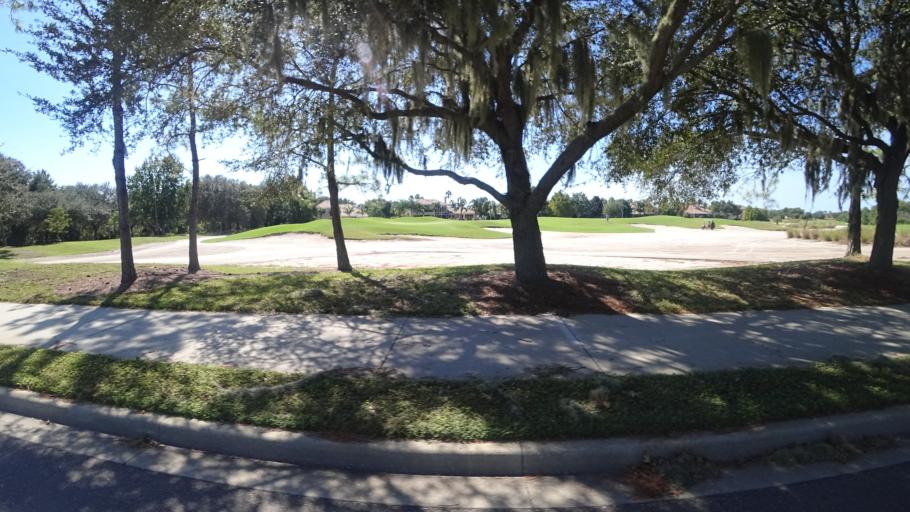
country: US
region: Florida
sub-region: Sarasota County
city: The Meadows
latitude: 27.3949
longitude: -82.4098
